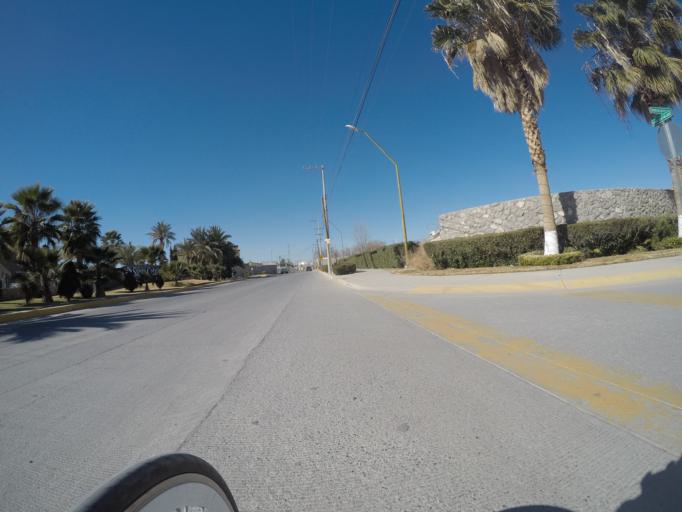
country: MX
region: Chihuahua
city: Ciudad Juarez
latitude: 31.6941
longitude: -106.3983
